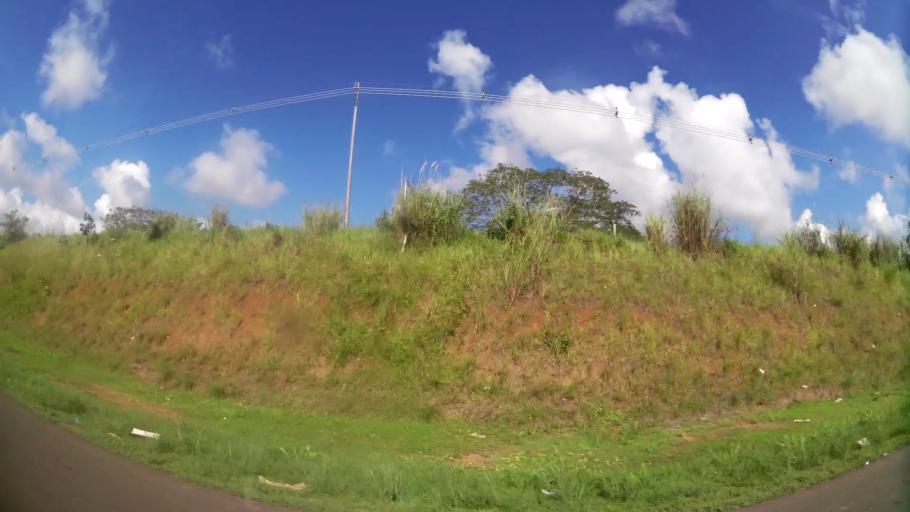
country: PA
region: Panama
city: Nuevo Arraijan
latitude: 8.8959
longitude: -79.7458
